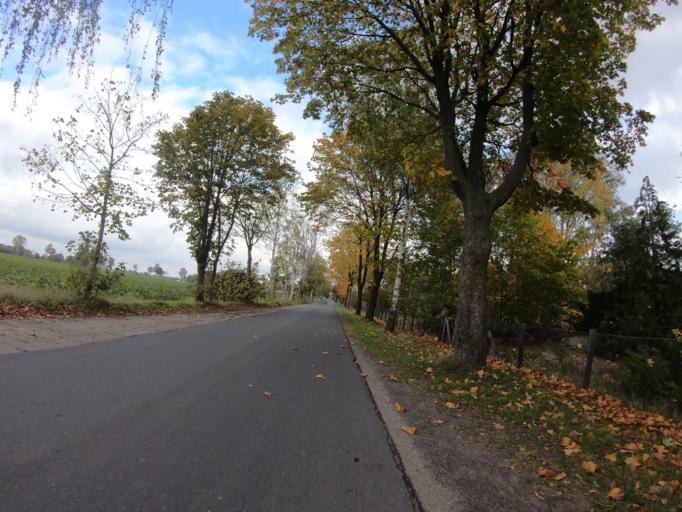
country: DE
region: Lower Saxony
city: Wahrenholz
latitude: 52.6056
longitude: 10.5929
